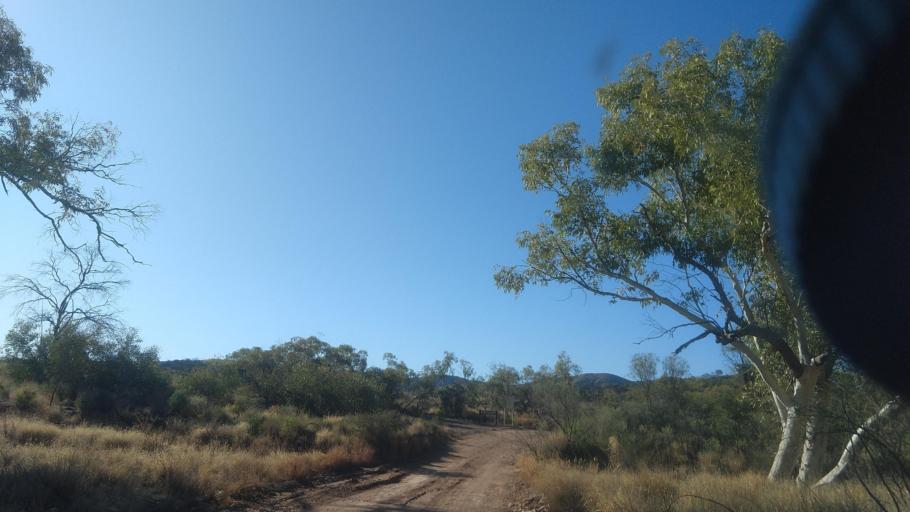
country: AU
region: Northern Territory
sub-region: Alice Springs
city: Alice Springs
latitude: -23.7525
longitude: 132.9183
